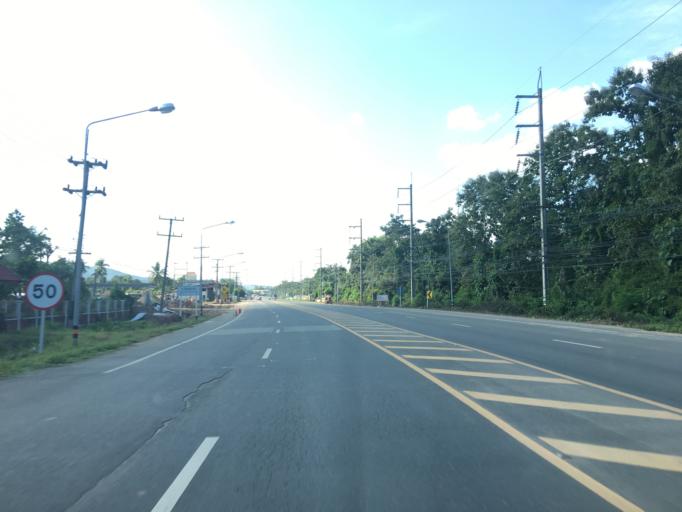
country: TH
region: Phayao
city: Chun
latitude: 19.3343
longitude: 100.1370
